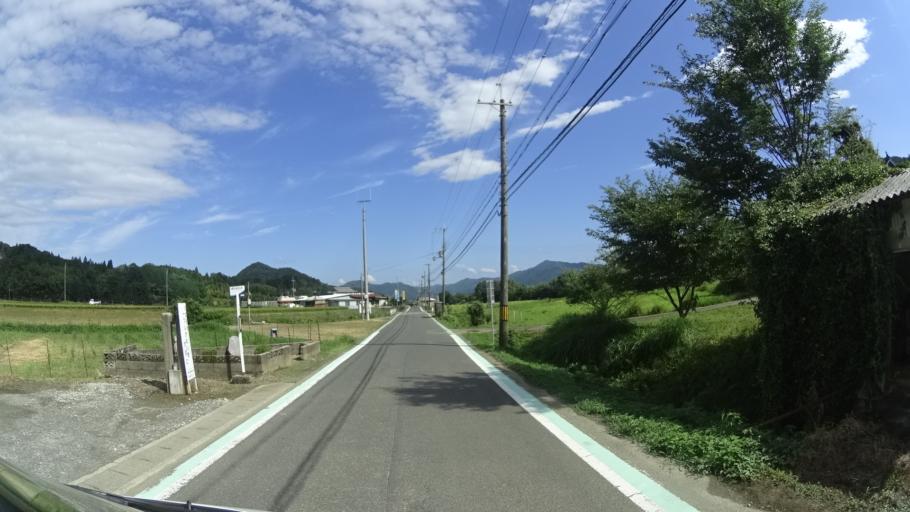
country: JP
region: Kyoto
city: Fukuchiyama
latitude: 35.3243
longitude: 135.1776
